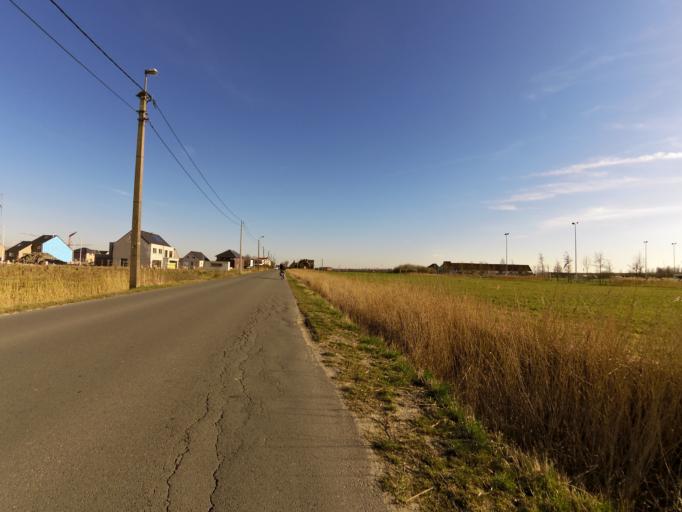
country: BE
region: Flanders
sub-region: Provincie West-Vlaanderen
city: Ostend
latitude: 51.2021
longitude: 2.9279
